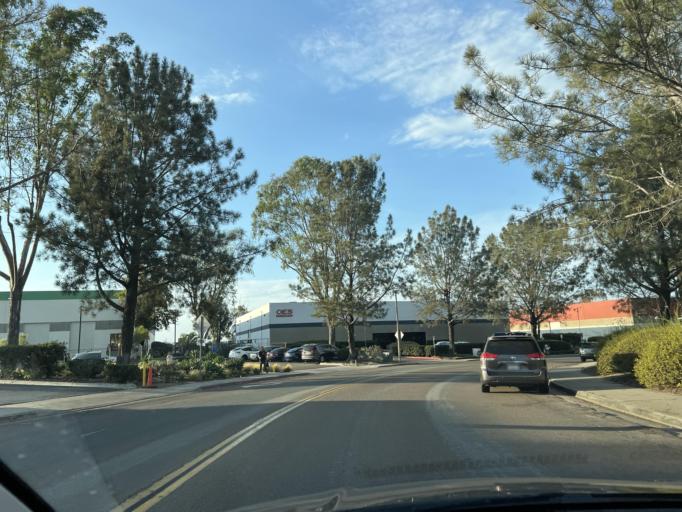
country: US
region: California
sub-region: San Diego County
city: Fairbanks Ranch
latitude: 32.8950
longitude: -117.1439
